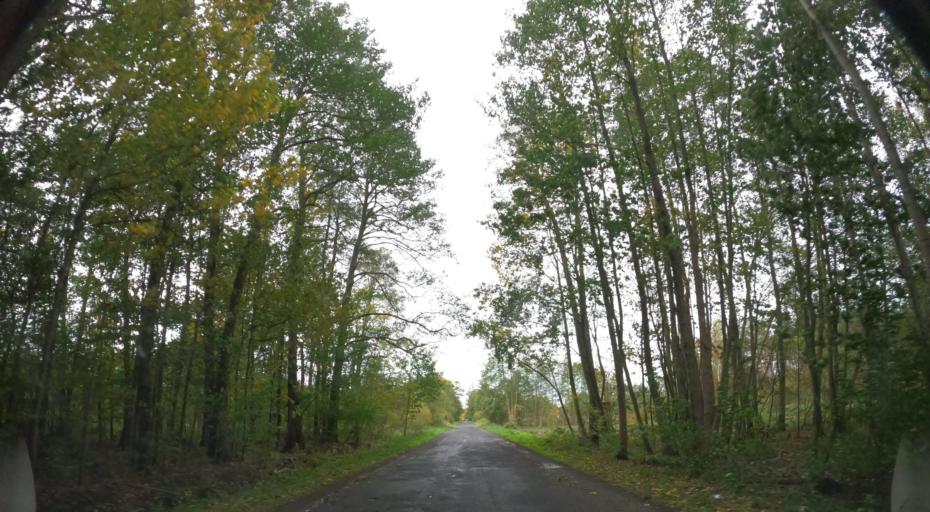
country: PL
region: West Pomeranian Voivodeship
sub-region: Powiat goleniowski
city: Stepnica
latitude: 53.6604
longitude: 14.6619
